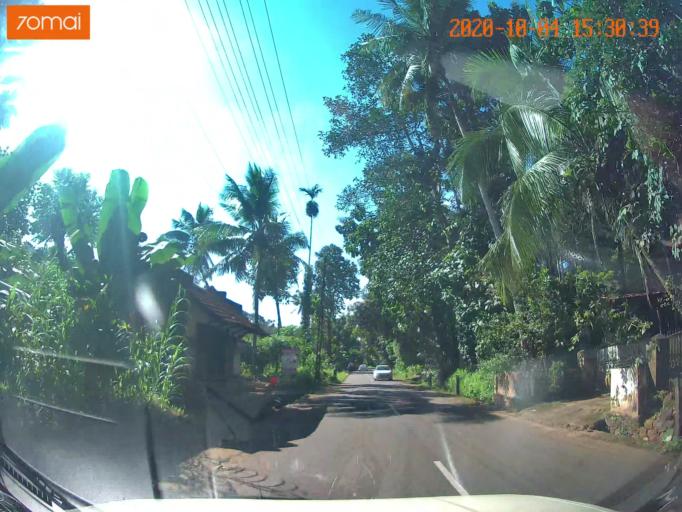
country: IN
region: Kerala
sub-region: Kottayam
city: Palackattumala
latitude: 9.7252
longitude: 76.6427
